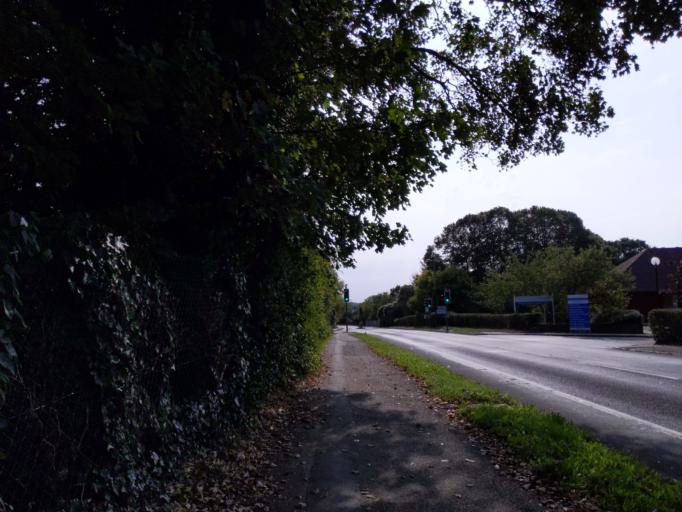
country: GB
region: England
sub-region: Oxfordshire
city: Cowley
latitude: 51.7176
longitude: -1.2281
